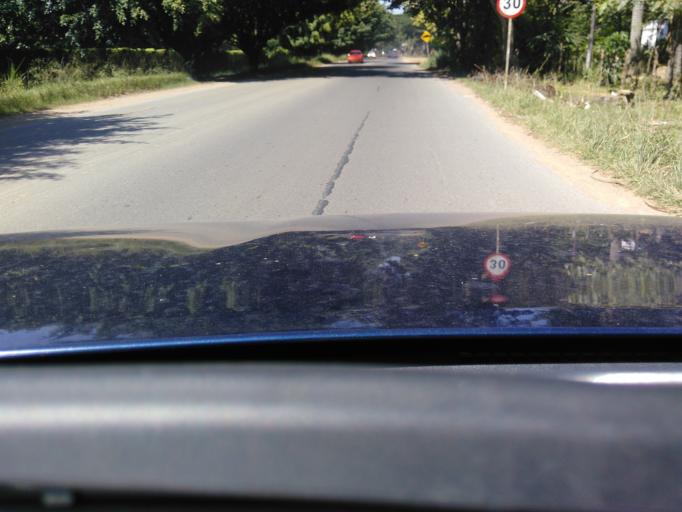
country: CO
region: Valle del Cauca
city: Jamundi
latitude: 3.2512
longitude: -76.5471
